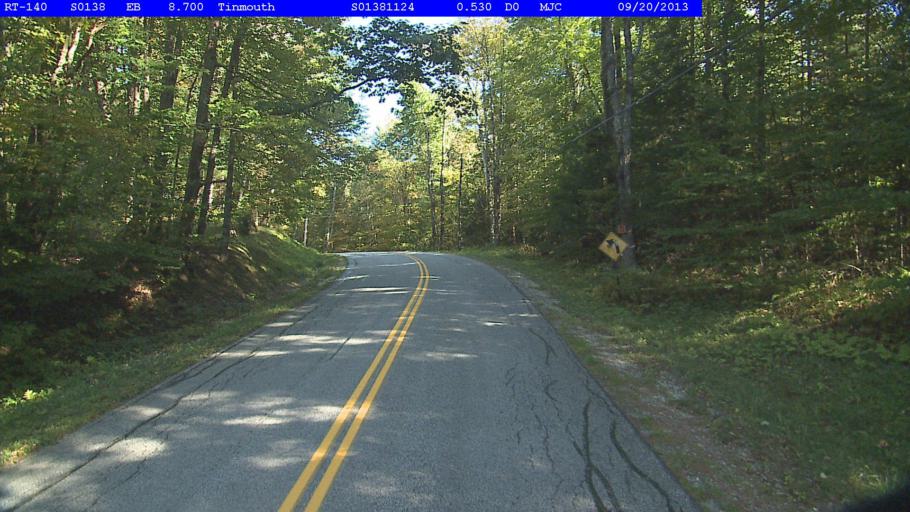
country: US
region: Vermont
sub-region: Rutland County
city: West Rutland
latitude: 43.4783
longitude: -73.0692
